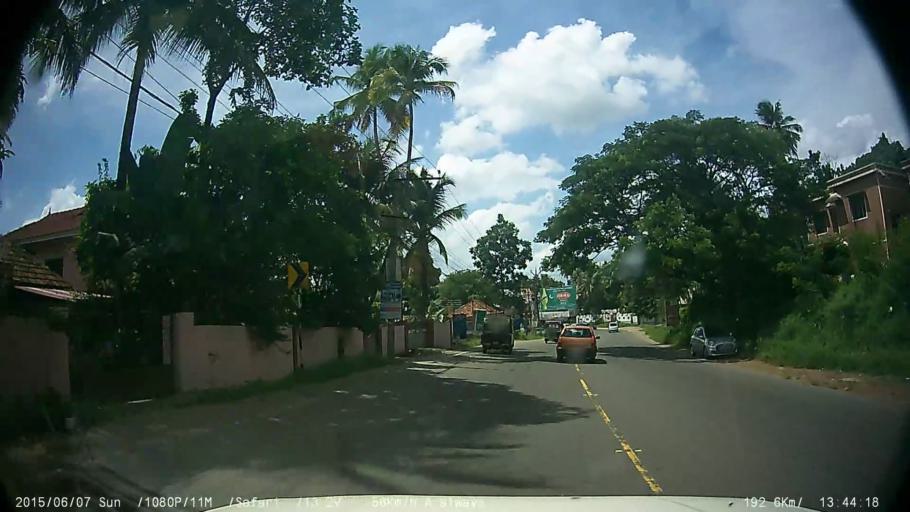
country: IN
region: Kerala
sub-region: Ernakulam
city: Perumpavur
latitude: 10.1241
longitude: 76.4731
